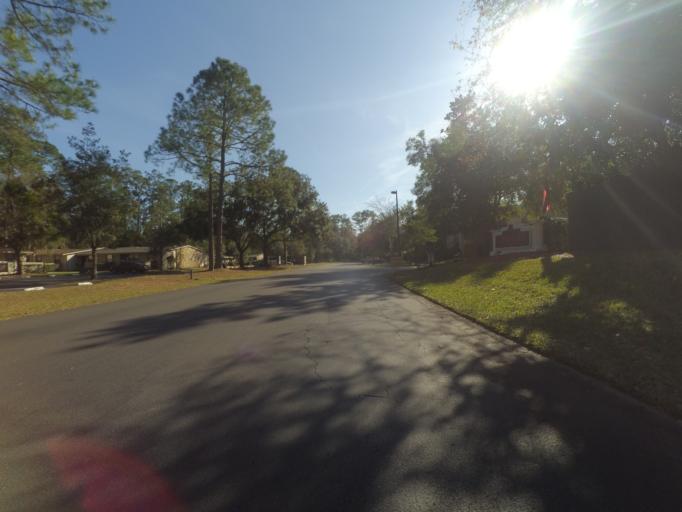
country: US
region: Florida
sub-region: Alachua County
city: Gainesville
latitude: 29.6187
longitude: -82.3575
